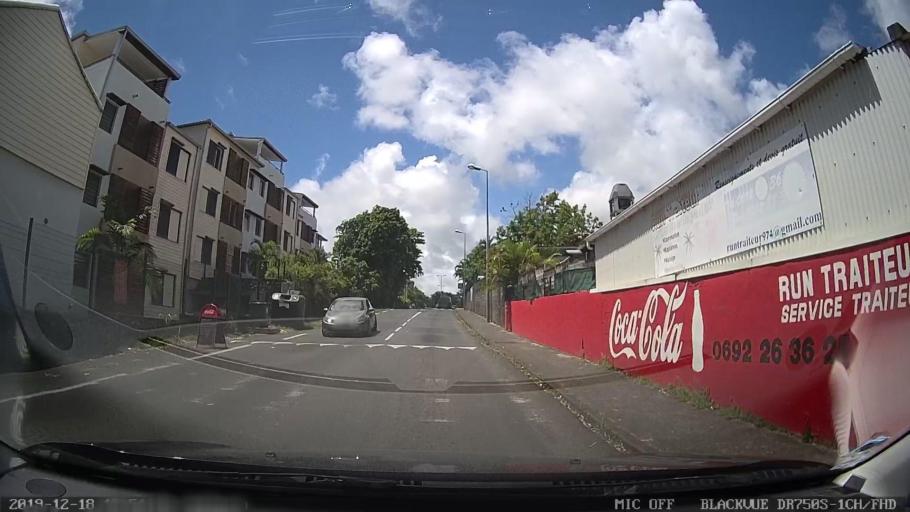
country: RE
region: Reunion
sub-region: Reunion
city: Saint-Andre
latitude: -20.9323
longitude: 55.6383
